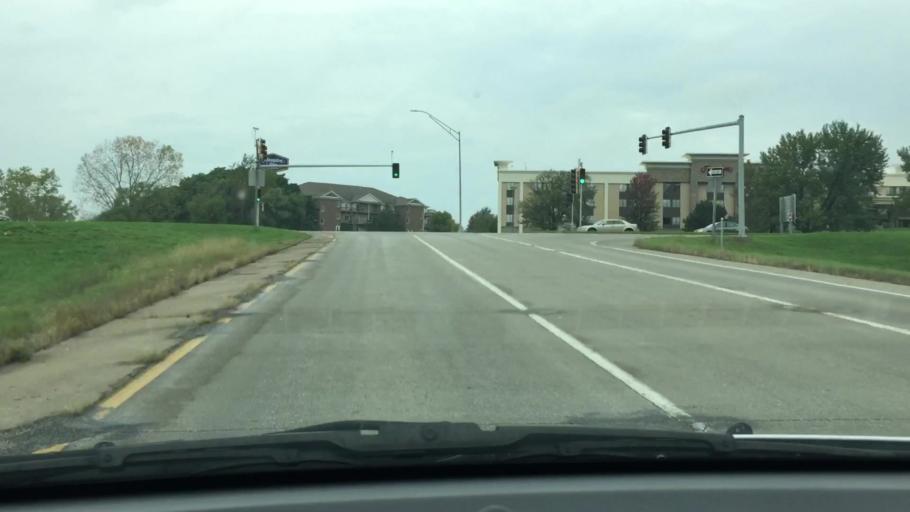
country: US
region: Iowa
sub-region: Johnson County
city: Coralville
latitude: 41.6866
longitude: -91.5638
